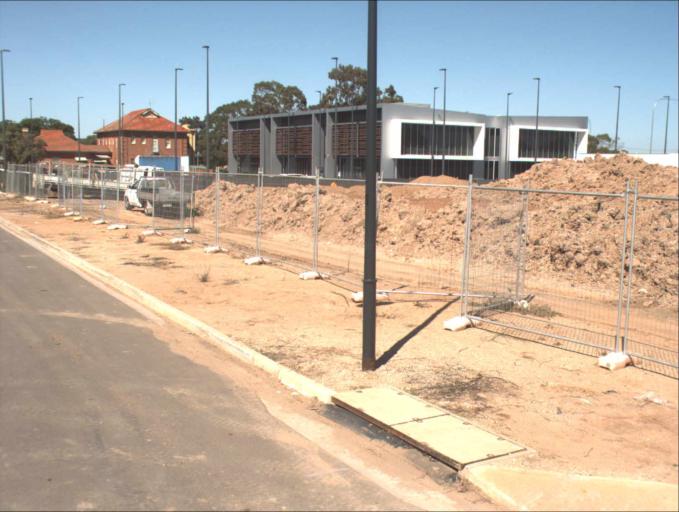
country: AU
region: South Australia
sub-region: Port Adelaide Enfield
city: Enfield
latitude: -34.8591
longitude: 138.6193
